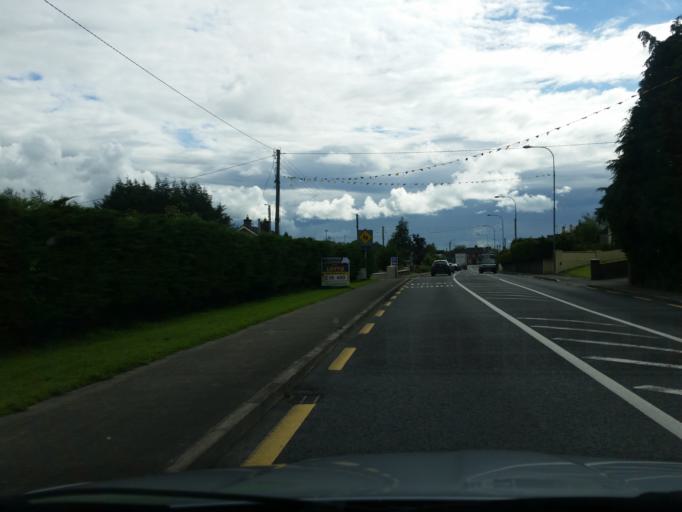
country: IE
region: Ulster
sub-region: An Cabhan
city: Cavan
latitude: 54.0475
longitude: -7.3761
